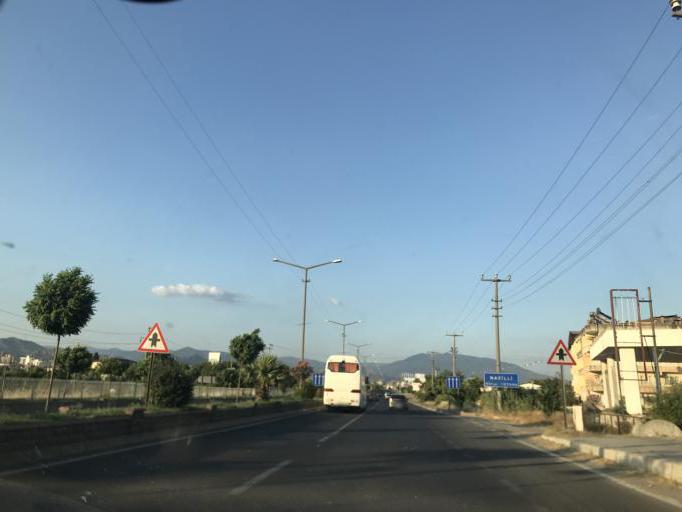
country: TR
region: Aydin
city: Nazilli
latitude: 37.9026
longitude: 28.2965
